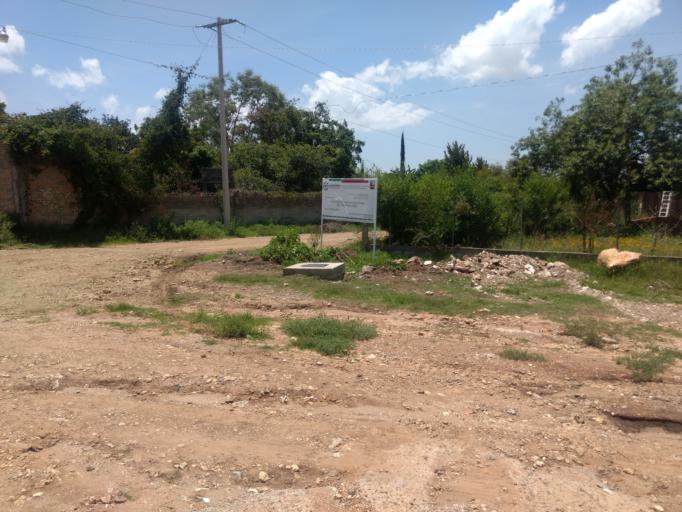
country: MX
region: Oaxaca
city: San Jeronimo Silacayoapilla
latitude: 17.8207
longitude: -97.8130
